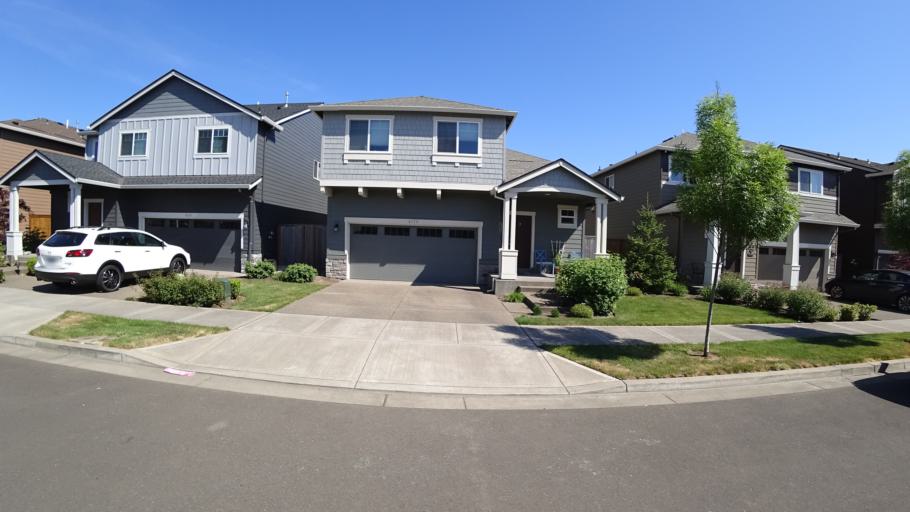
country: US
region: Oregon
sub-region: Washington County
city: Rockcreek
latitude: 45.5261
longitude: -122.9174
